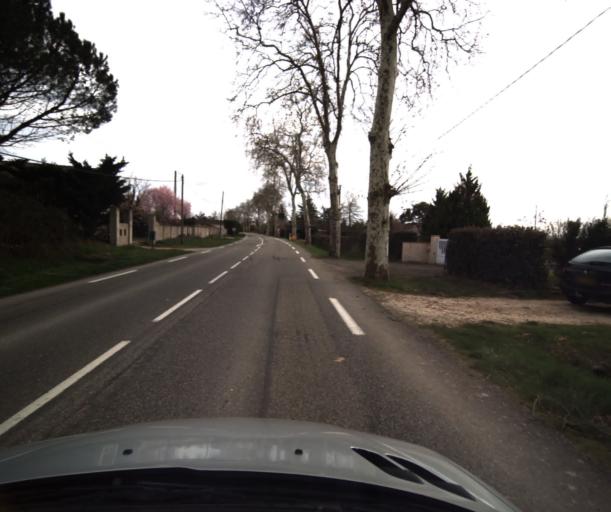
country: FR
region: Midi-Pyrenees
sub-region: Departement du Tarn-et-Garonne
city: Montbeton
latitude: 44.0541
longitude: 1.2935
